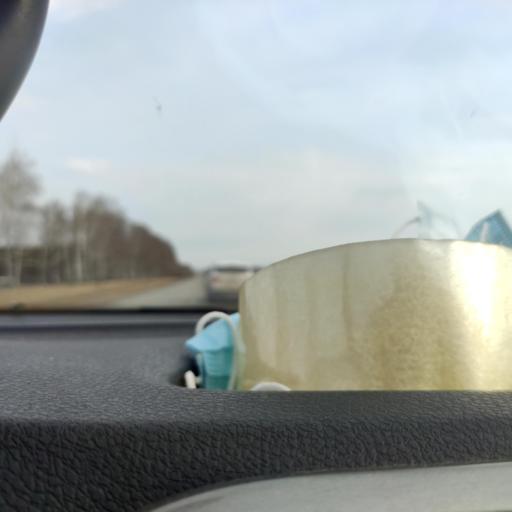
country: RU
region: Bashkortostan
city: Ulukulevo
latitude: 54.3792
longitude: 56.3914
